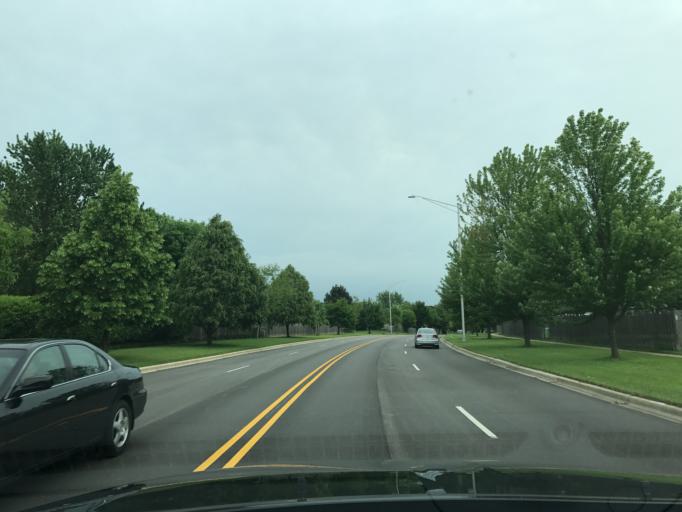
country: US
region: Illinois
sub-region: DuPage County
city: Woodridge
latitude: 41.7417
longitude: -88.1028
